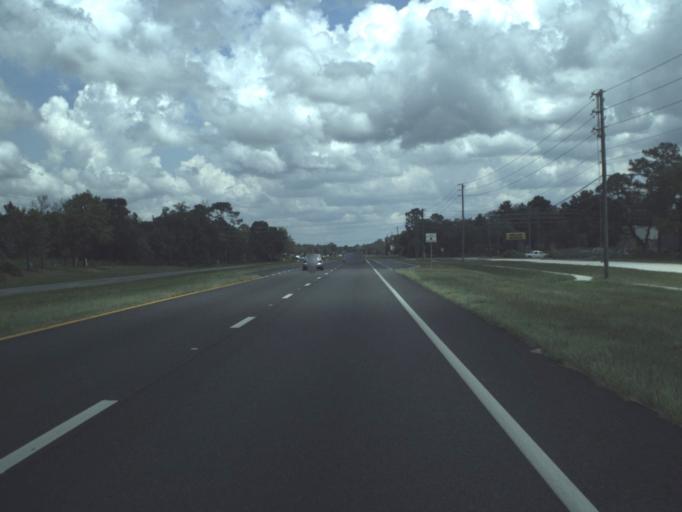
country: US
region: Florida
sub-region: Hernando County
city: North Weeki Wachee
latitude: 28.5823
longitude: -82.5551
